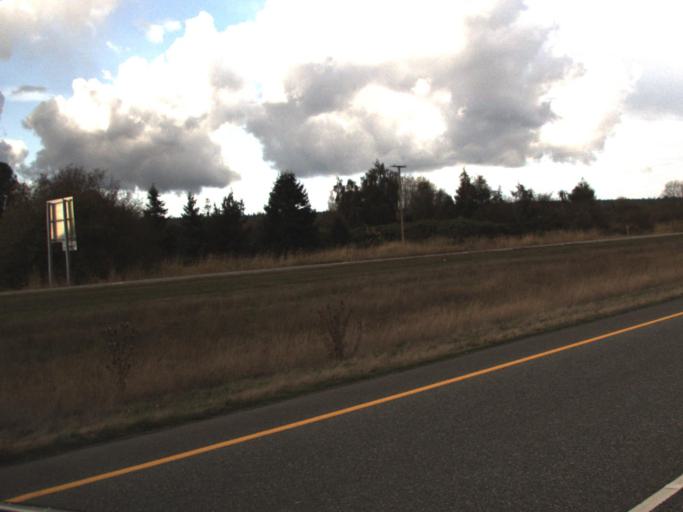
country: US
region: Washington
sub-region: Skagit County
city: Anacortes
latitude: 48.4497
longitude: -122.4818
